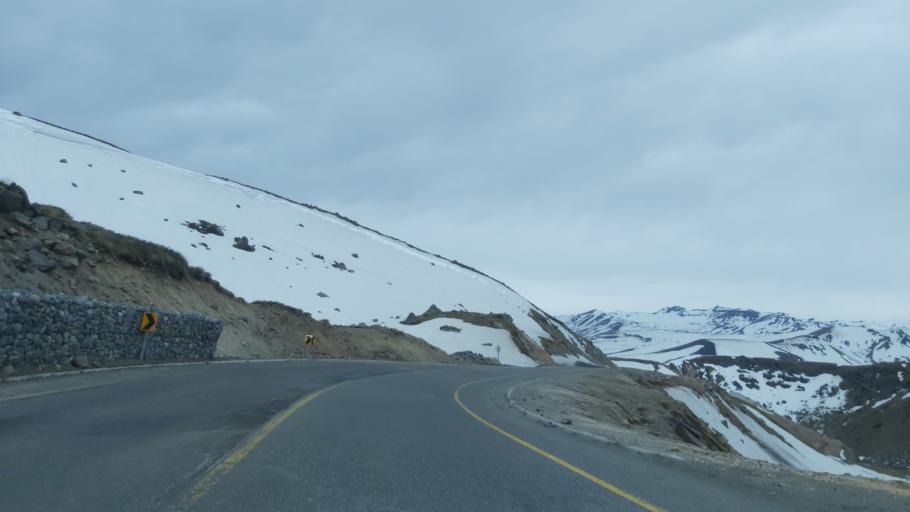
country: CL
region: Maule
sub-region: Provincia de Linares
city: Colbun
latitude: -35.9963
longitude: -70.5601
